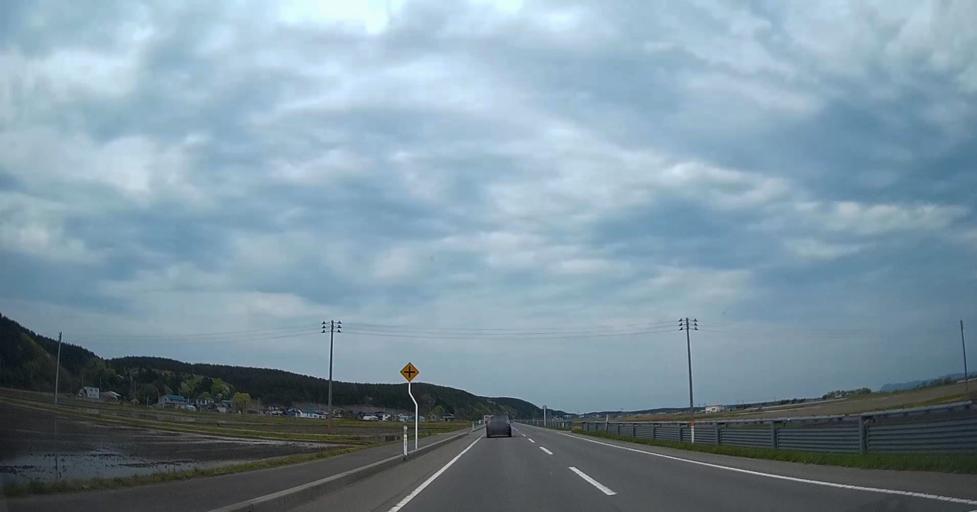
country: JP
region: Aomori
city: Shimokizukuri
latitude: 40.9929
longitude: 140.3623
